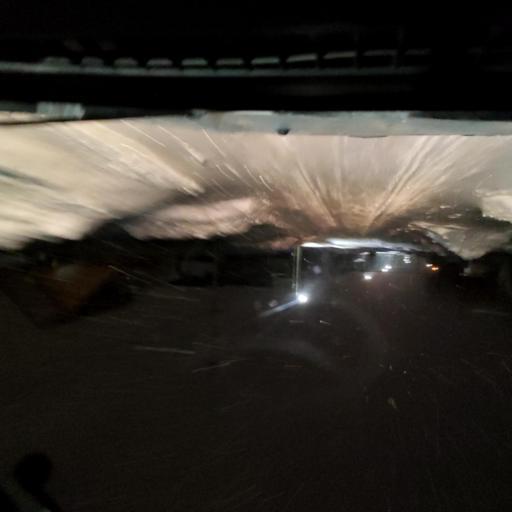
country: RU
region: Bashkortostan
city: Iglino
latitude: 54.8239
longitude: 56.3833
